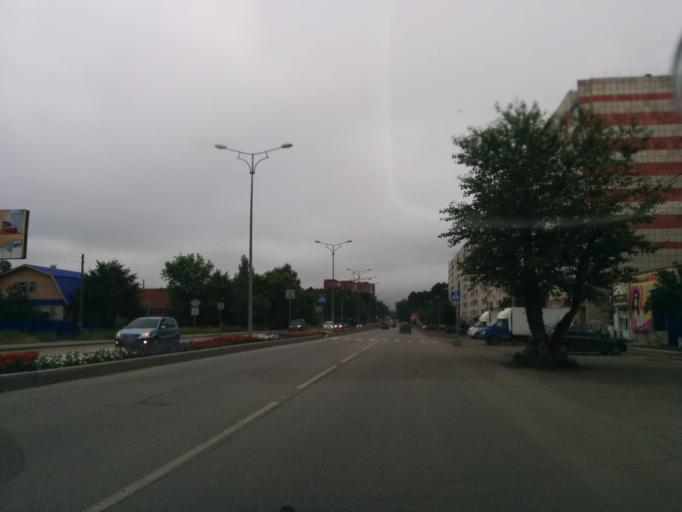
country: RU
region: Perm
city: Kondratovo
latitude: 58.0280
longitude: 56.0032
